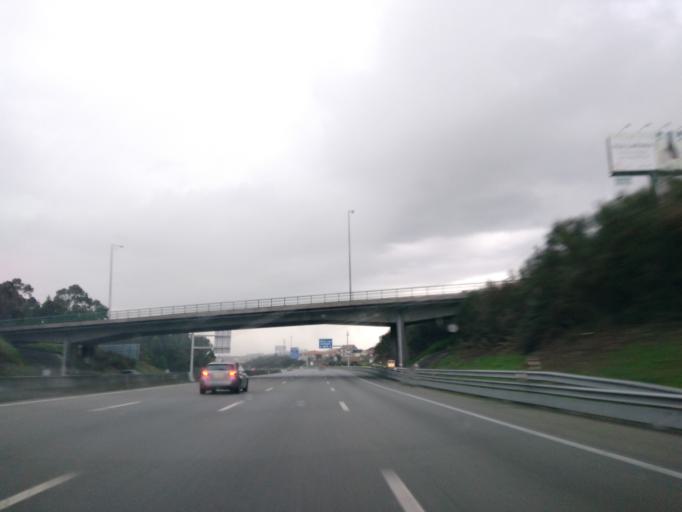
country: PT
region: Porto
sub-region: Maia
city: Aguas Santas
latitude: 41.2122
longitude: -8.5783
